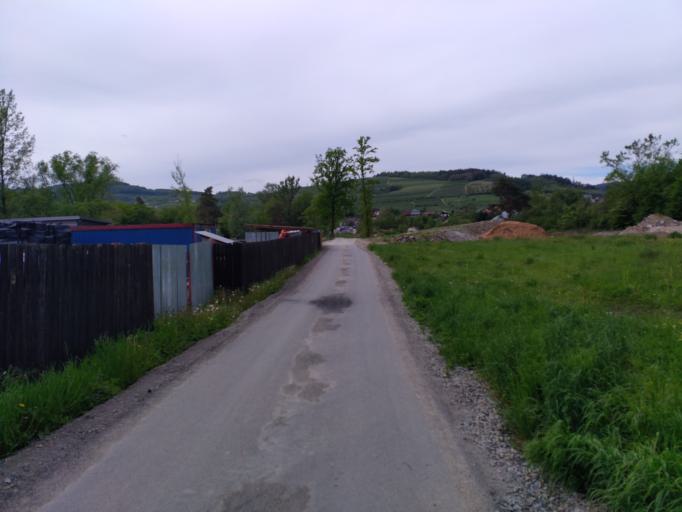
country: PL
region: Lesser Poland Voivodeship
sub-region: Powiat nowosadecki
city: Lacko
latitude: 49.5502
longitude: 20.4312
